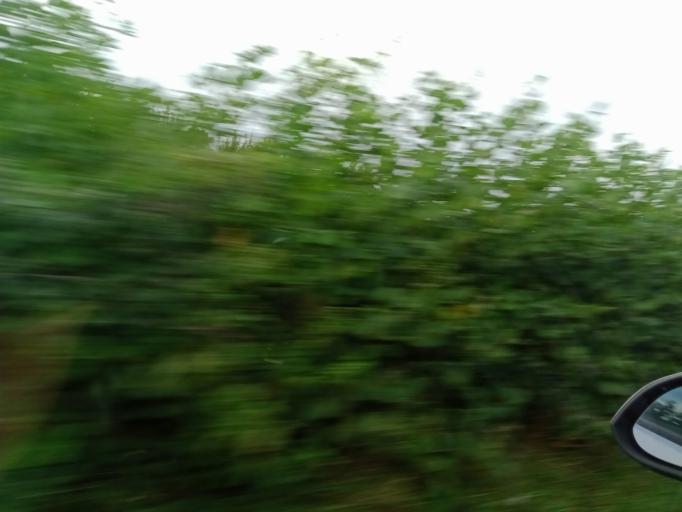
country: IE
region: Leinster
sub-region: Laois
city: Portlaoise
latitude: 53.0526
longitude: -7.3074
